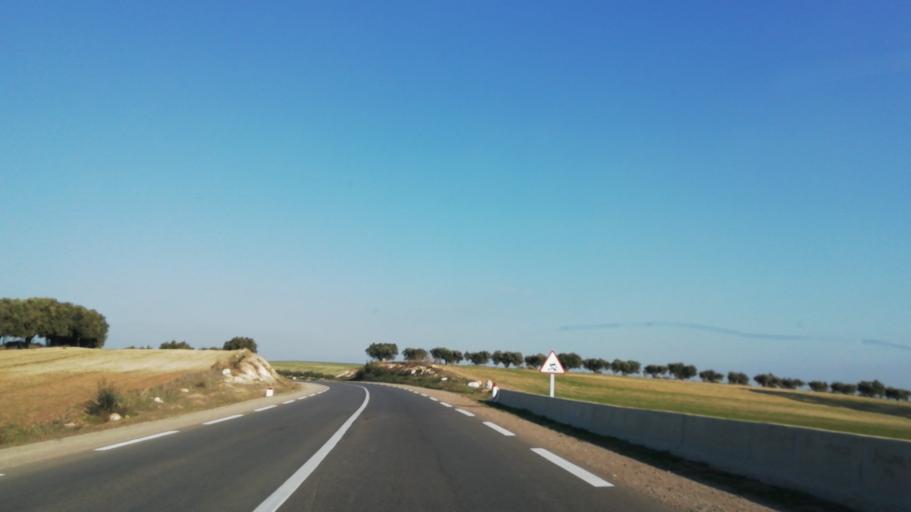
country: DZ
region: Sidi Bel Abbes
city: Sidi Bel Abbes
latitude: 35.1625
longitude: -0.8653
